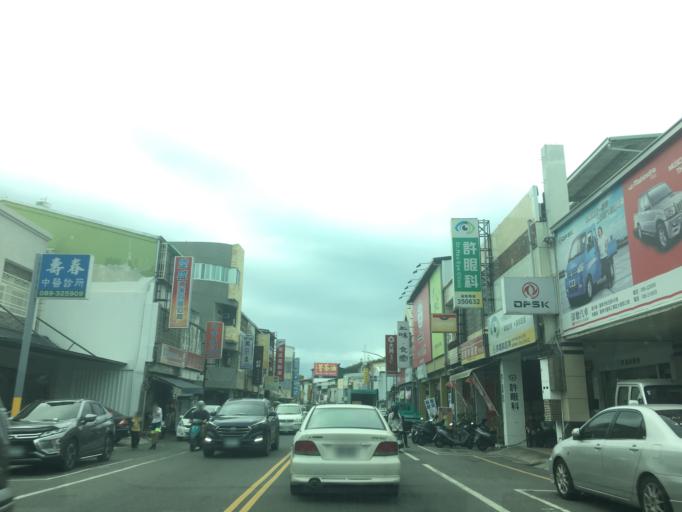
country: TW
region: Taiwan
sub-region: Taitung
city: Taitung
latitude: 22.7601
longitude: 121.1393
